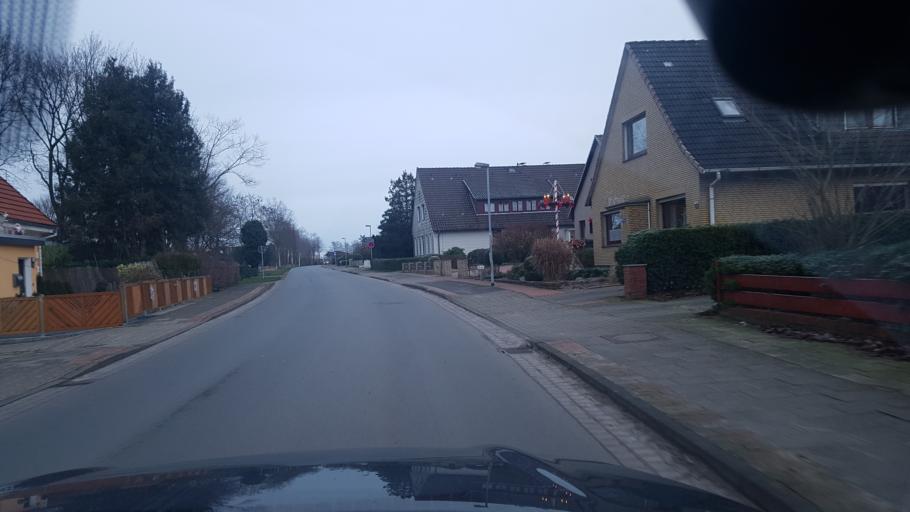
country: DE
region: Lower Saxony
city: Langen
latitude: 53.6073
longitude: 8.6694
